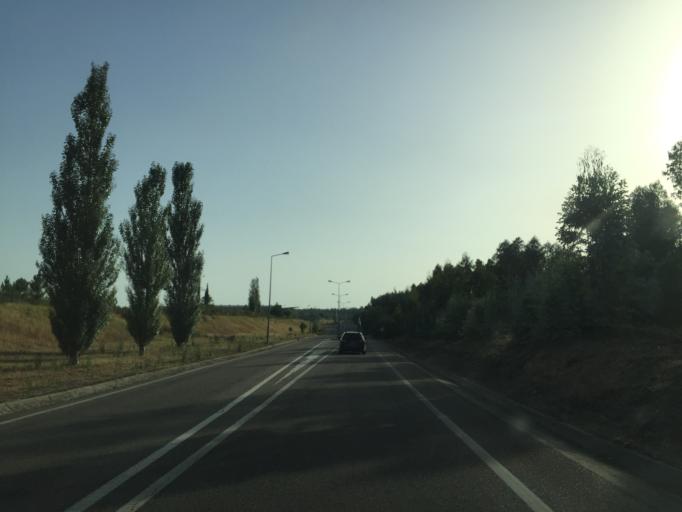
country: PT
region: Santarem
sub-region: Chamusca
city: Vila Nova da Barquinha
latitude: 39.5027
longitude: -8.4270
